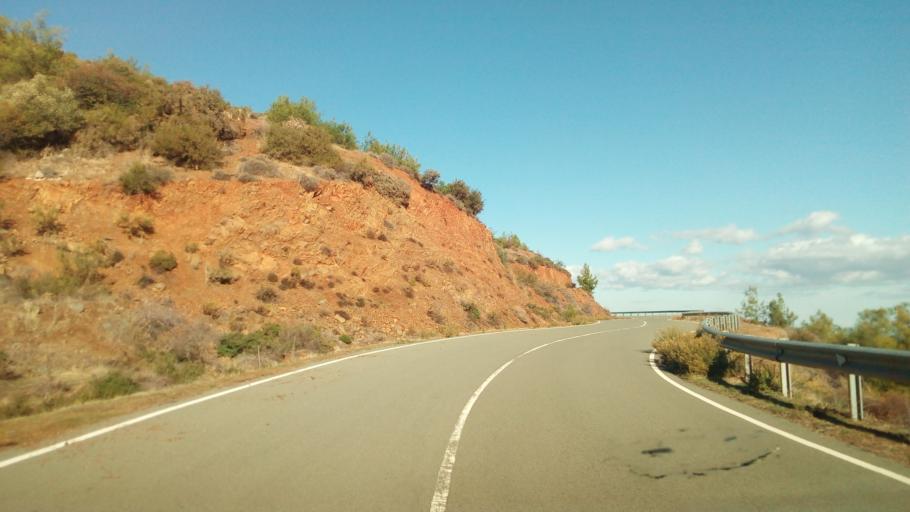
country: CY
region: Lefkosia
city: Lefka
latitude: 35.1034
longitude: 32.7535
